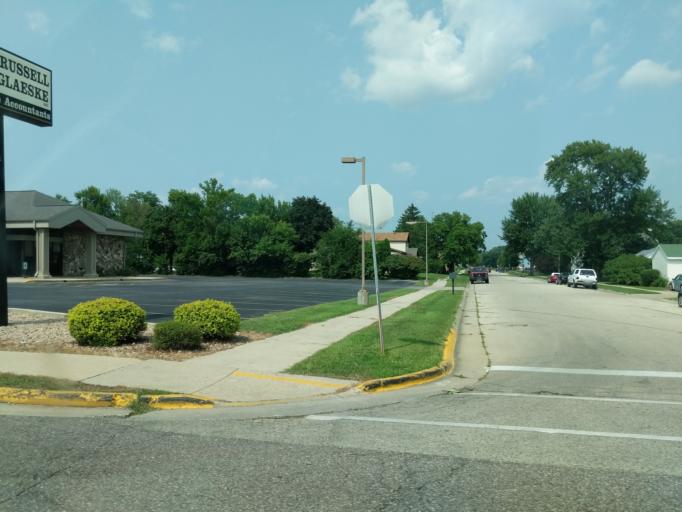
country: US
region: Wisconsin
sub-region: Columbia County
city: Portage
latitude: 43.5363
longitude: -89.4517
